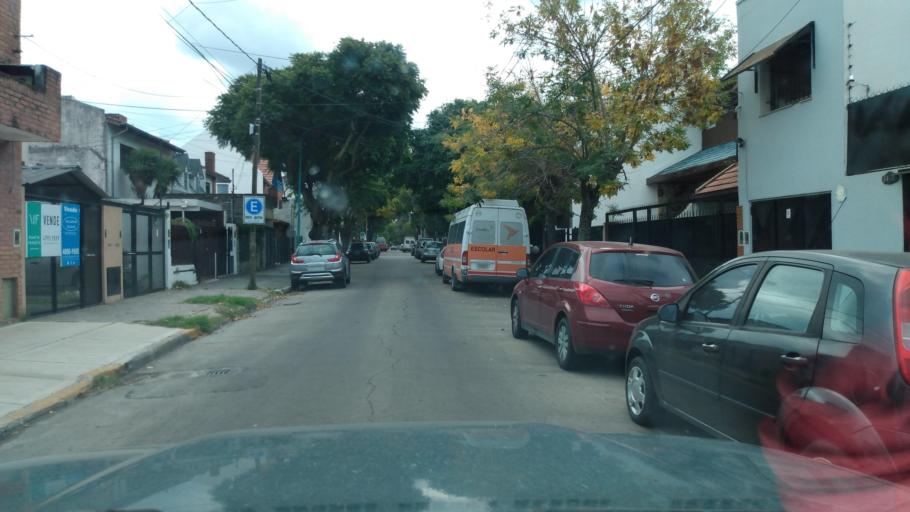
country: AR
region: Buenos Aires
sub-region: Partido de Vicente Lopez
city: Olivos
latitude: -34.5080
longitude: -58.4995
